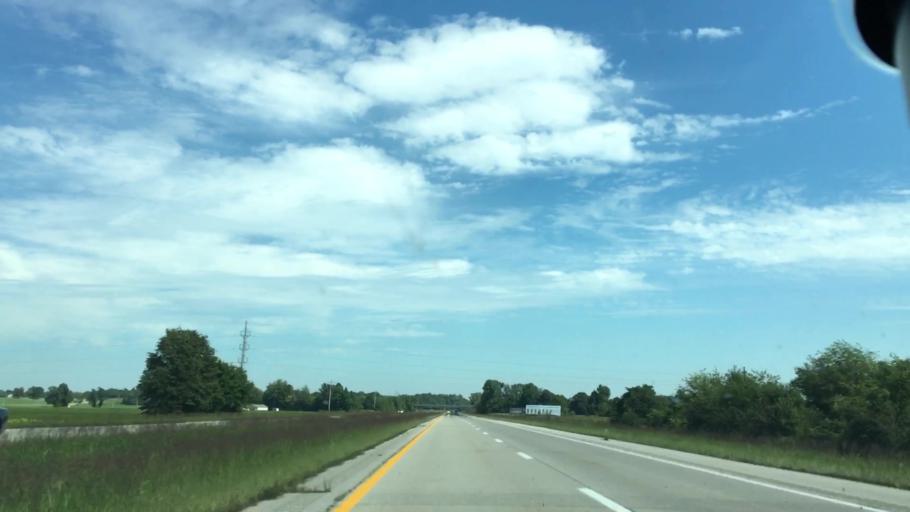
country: US
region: Kentucky
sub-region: Daviess County
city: Owensboro
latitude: 37.7649
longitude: -87.2216
